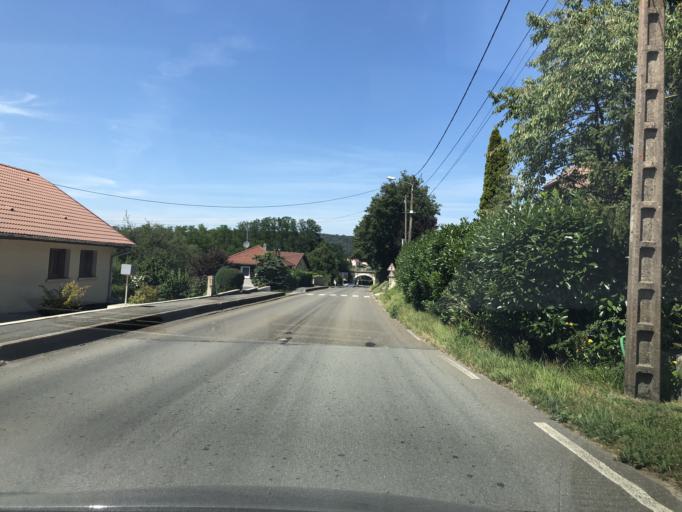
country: FR
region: Franche-Comte
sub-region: Departement du Doubs
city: Voujeaucourt
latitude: 47.4659
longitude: 6.7653
